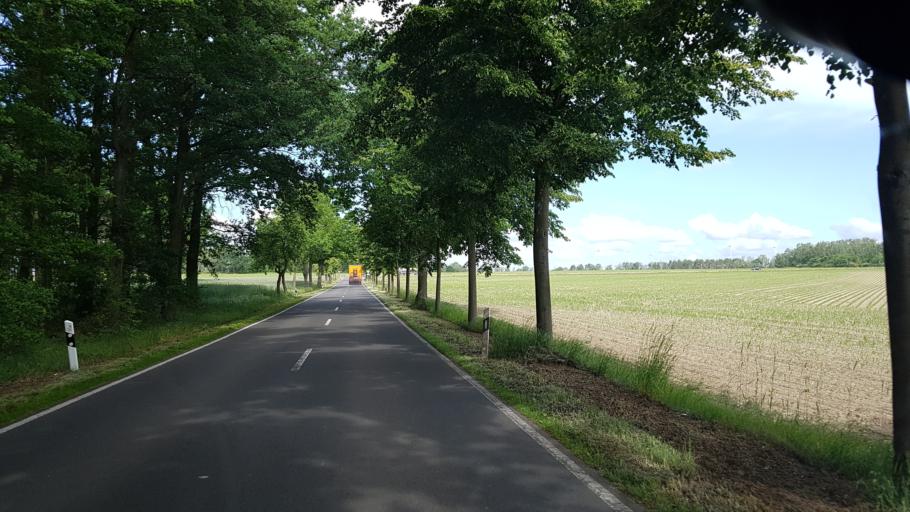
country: DE
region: Brandenburg
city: Luckau
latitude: 51.8230
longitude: 13.6873
